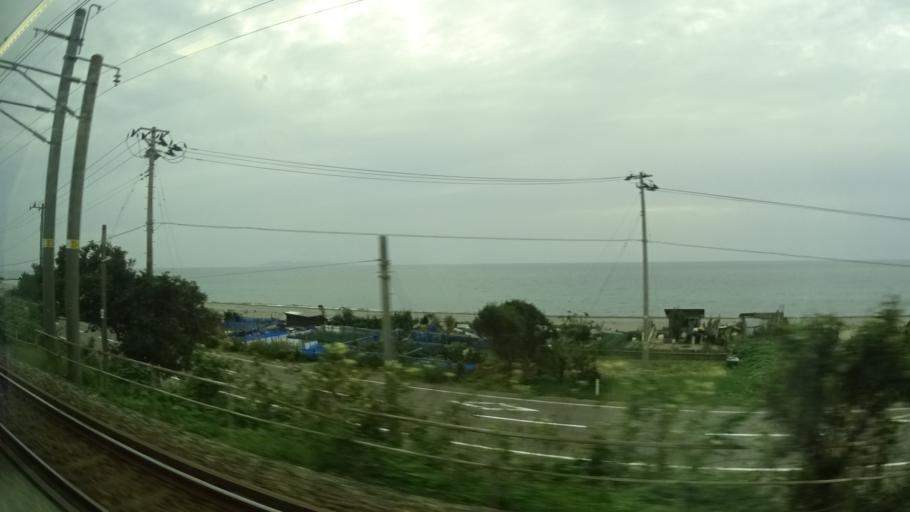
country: JP
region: Niigata
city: Murakami
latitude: 38.5253
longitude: 139.5401
